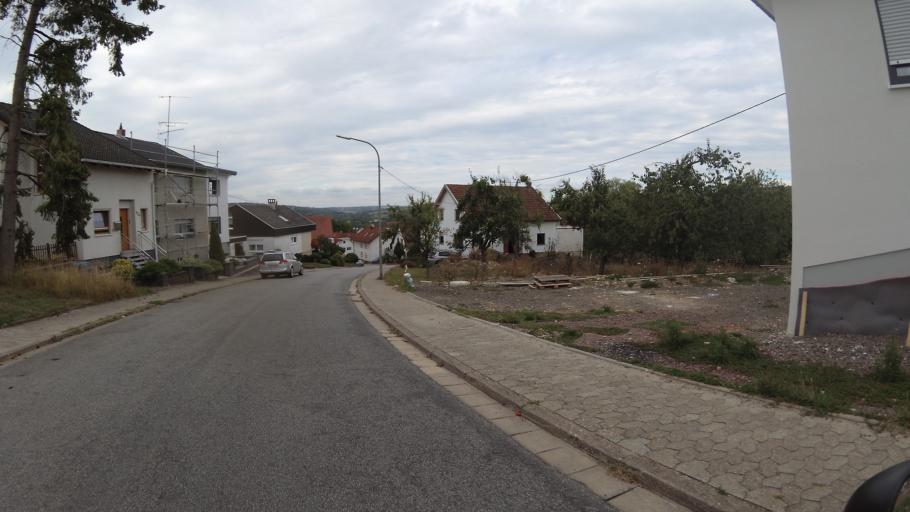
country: DE
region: Saarland
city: Kleinblittersdorf
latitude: 49.1436
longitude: 7.0549
